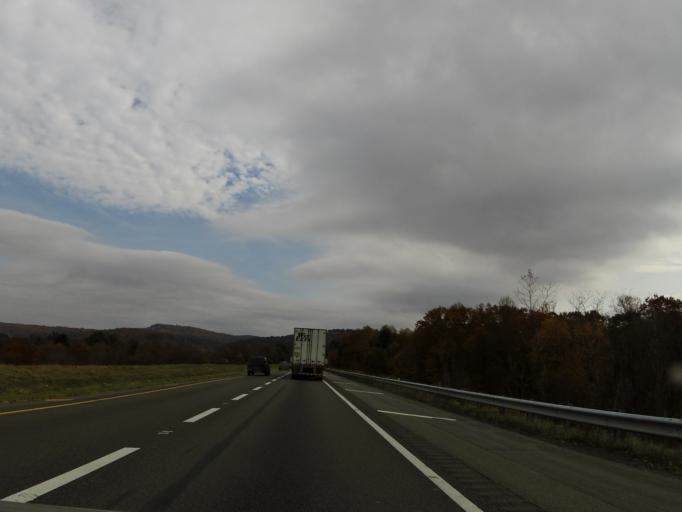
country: US
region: Virginia
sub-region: Carroll County
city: Hillsville
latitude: 36.6824
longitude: -80.7175
